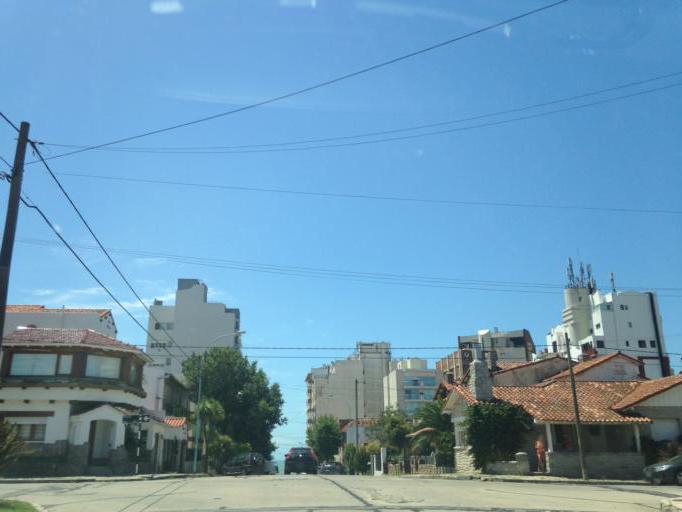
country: AR
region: Buenos Aires
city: Mar del Plata
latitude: -38.0153
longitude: -57.5343
